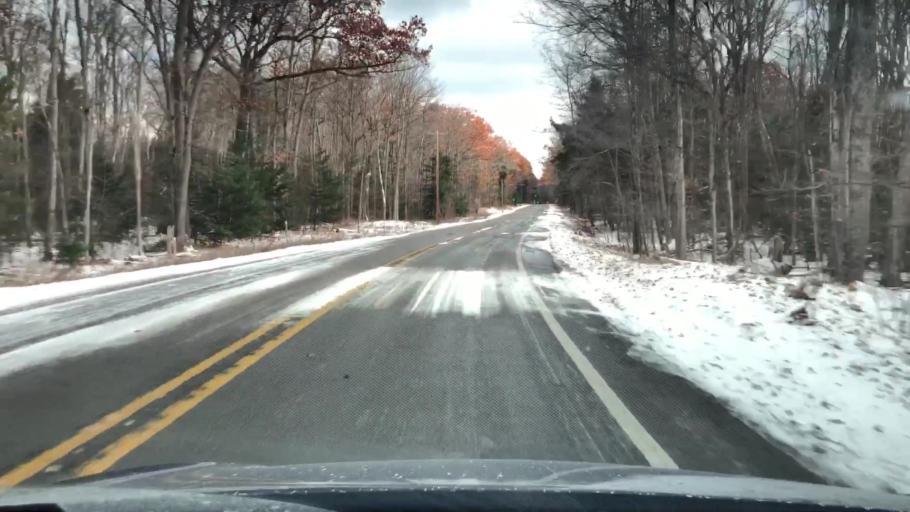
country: US
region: Michigan
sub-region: Antrim County
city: Elk Rapids
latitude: 44.9898
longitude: -85.4899
